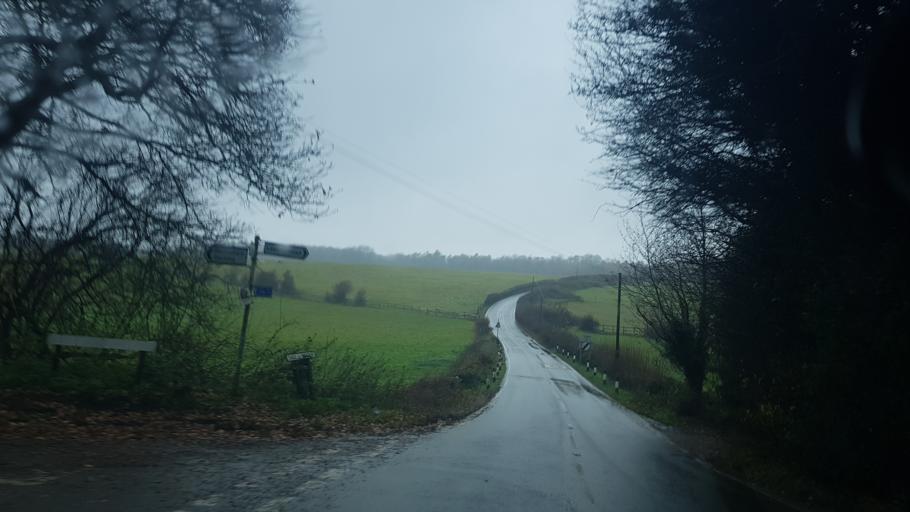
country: GB
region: England
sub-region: Surrey
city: Headley
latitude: 51.2753
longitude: -0.2820
